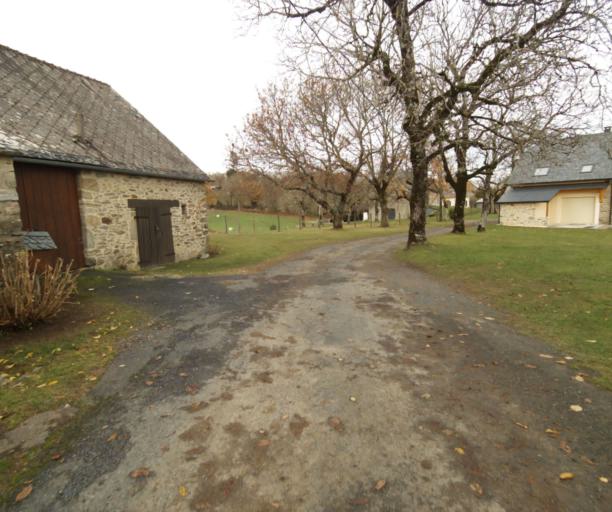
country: FR
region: Limousin
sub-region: Departement de la Correze
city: Sainte-Fortunade
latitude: 45.1744
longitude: 1.7681
